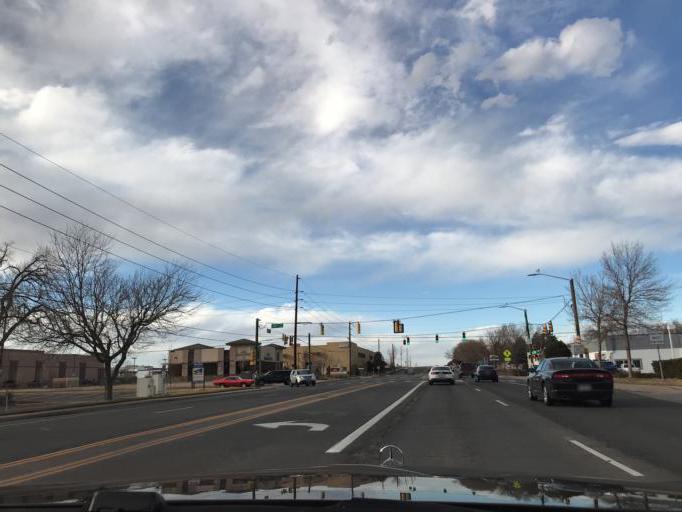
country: US
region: Colorado
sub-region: Jefferson County
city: Applewood
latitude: 39.7901
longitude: -105.1380
